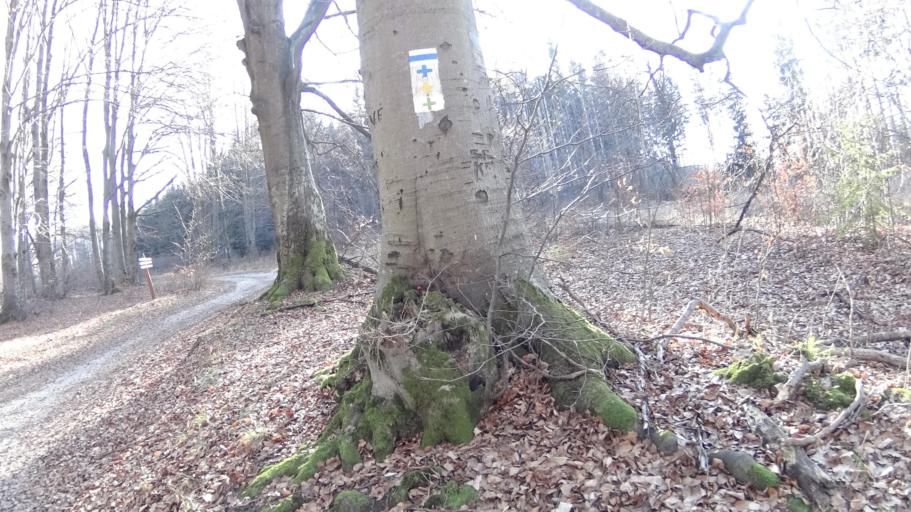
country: HU
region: Heves
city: Szilvasvarad
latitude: 48.0951
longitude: 20.4818
